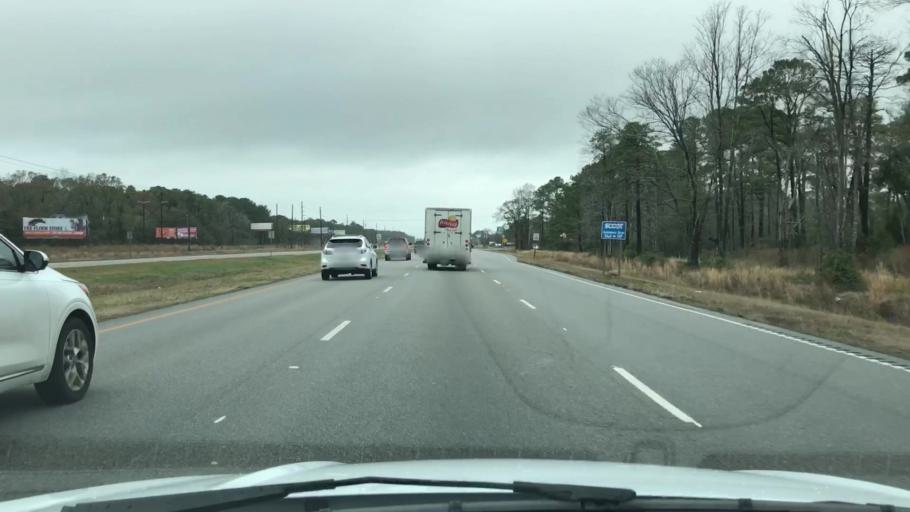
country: US
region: South Carolina
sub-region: Horry County
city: Forestbrook
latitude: 33.7697
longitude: -78.9778
